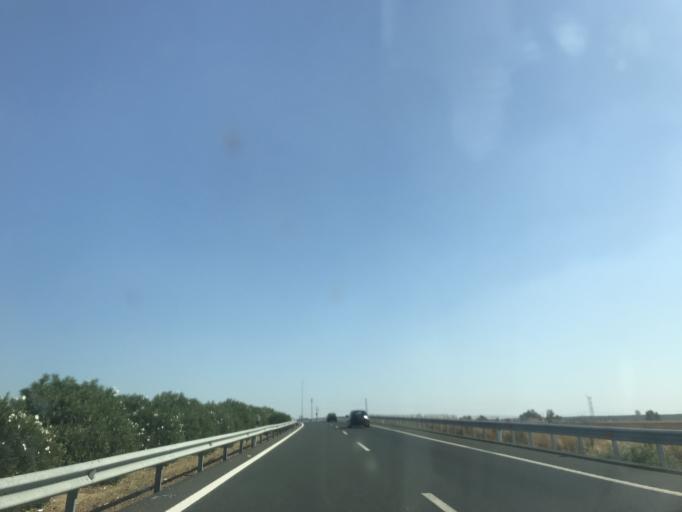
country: ES
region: Andalusia
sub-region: Provincia de Sevilla
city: Mairena del Alcor
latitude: 37.3186
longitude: -5.7647
